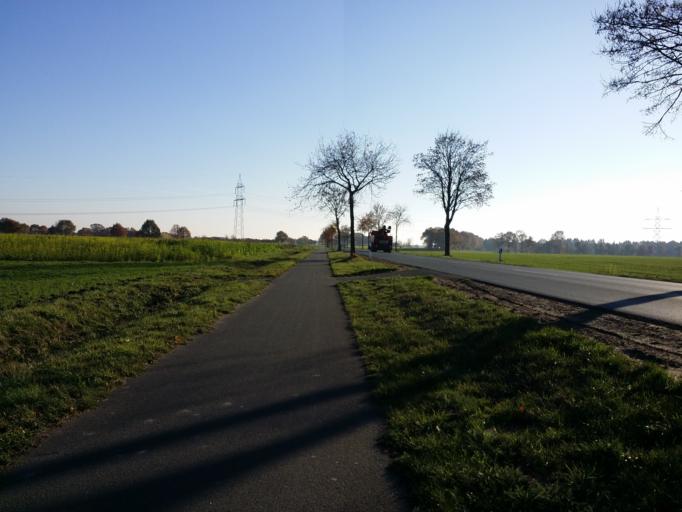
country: DE
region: Lower Saxony
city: Langwedel
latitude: 53.0248
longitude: 9.1642
